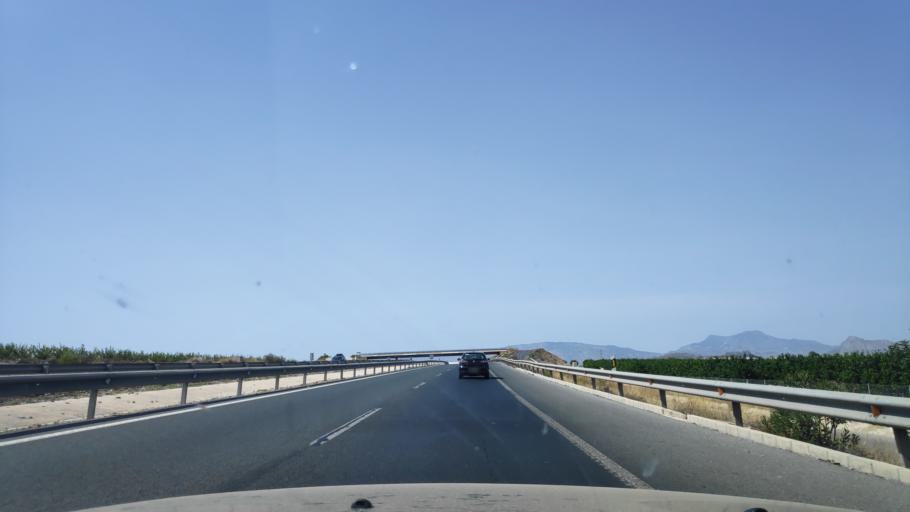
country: ES
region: Murcia
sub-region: Murcia
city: Lorqui
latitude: 38.1088
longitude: -1.2384
